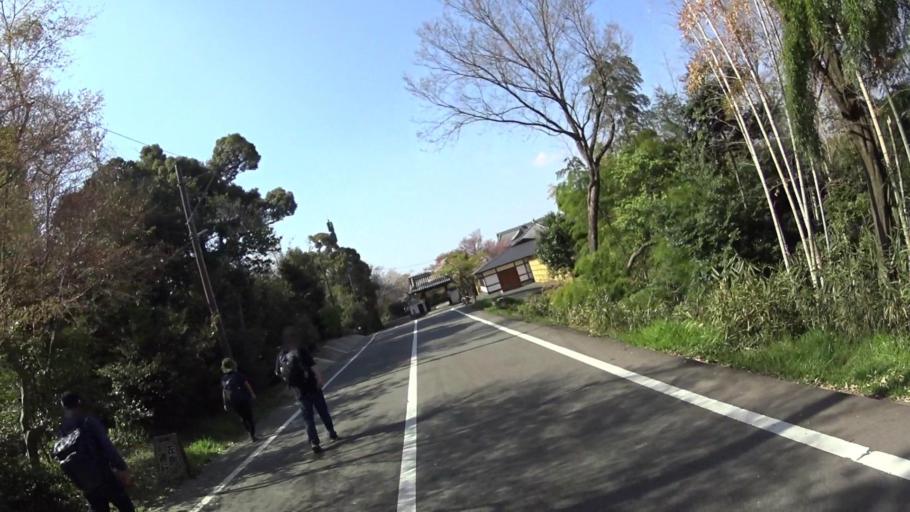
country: JP
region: Kyoto
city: Kyoto
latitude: 35.0008
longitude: 135.7880
